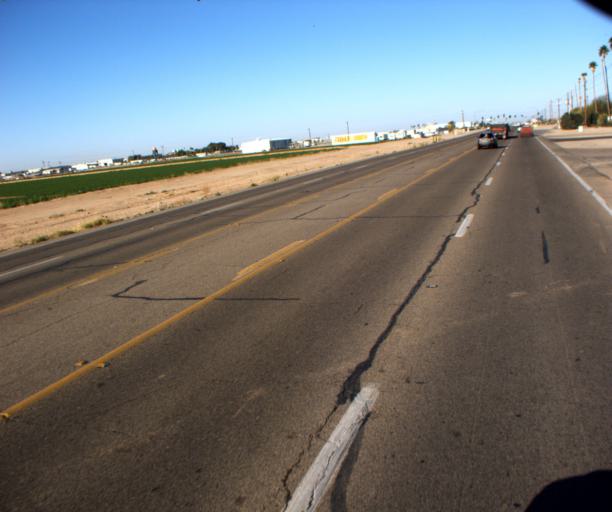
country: US
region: Arizona
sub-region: Yuma County
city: Yuma
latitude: 32.6699
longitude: -114.5604
